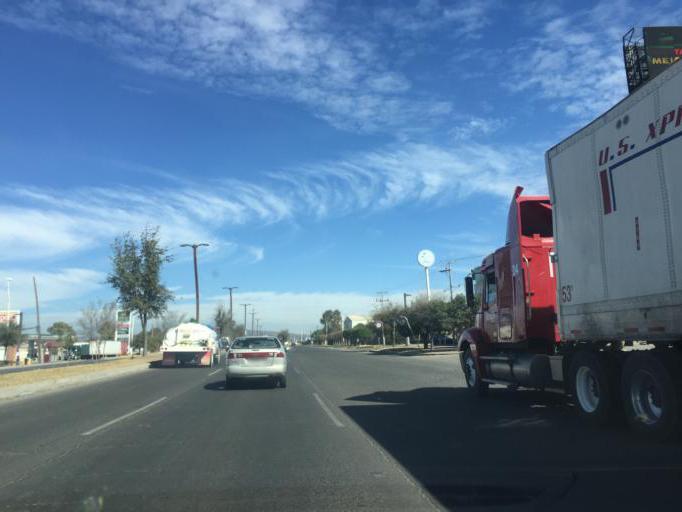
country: MX
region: Queretaro
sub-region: San Juan del Rio
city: Santa Cruz Escandon
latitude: 20.4136
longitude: -99.9812
